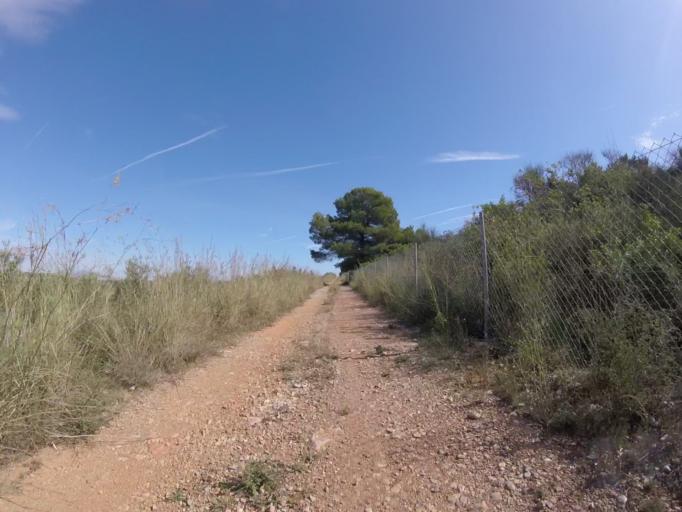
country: ES
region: Valencia
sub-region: Provincia de Castello
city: Peniscola
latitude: 40.3918
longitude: 0.3554
